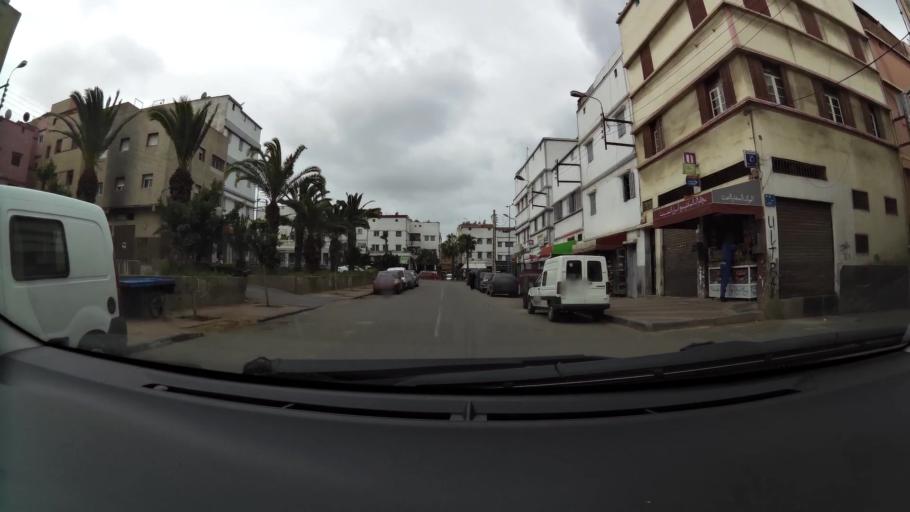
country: MA
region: Grand Casablanca
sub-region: Casablanca
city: Casablanca
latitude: 33.5632
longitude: -7.5667
